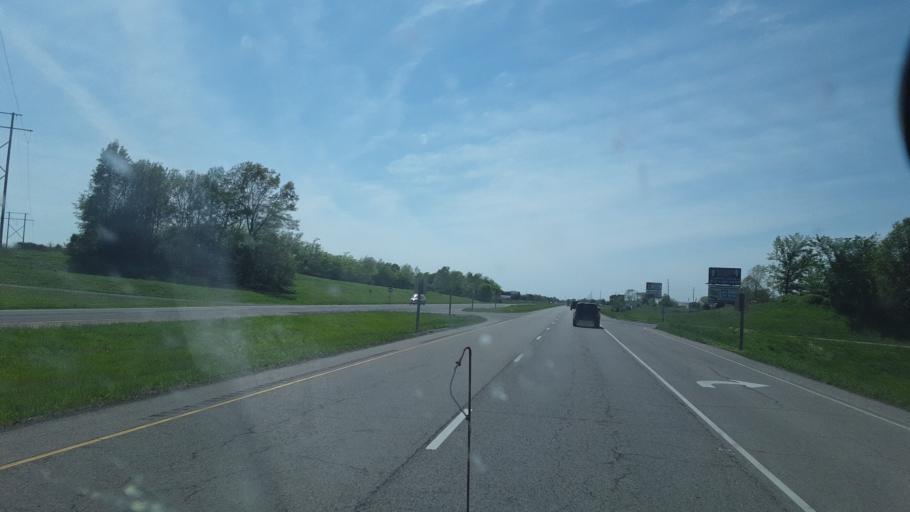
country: US
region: Illinois
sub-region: Williamson County
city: Marion
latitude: 37.7298
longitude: -88.8265
